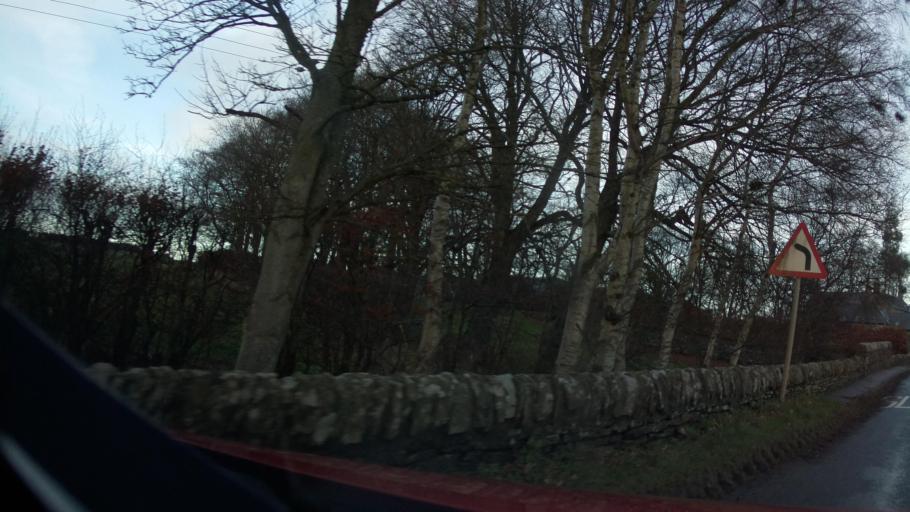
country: GB
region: Scotland
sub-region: Angus
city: Letham
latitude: 56.5382
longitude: -2.7879
